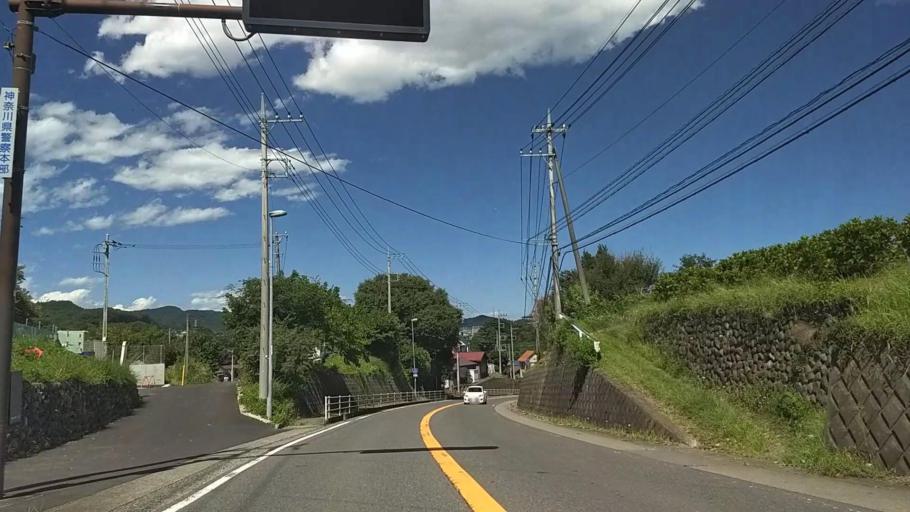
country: JP
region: Tokyo
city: Hachioji
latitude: 35.5626
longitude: 139.2645
